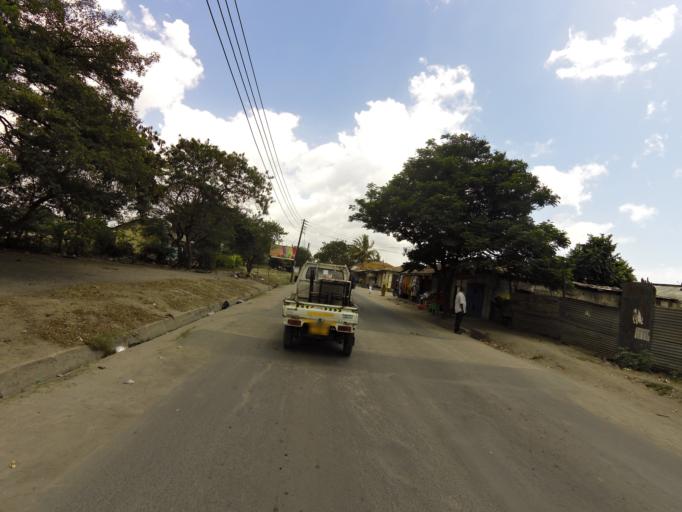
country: TZ
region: Dar es Salaam
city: Magomeni
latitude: -6.8022
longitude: 39.2575
